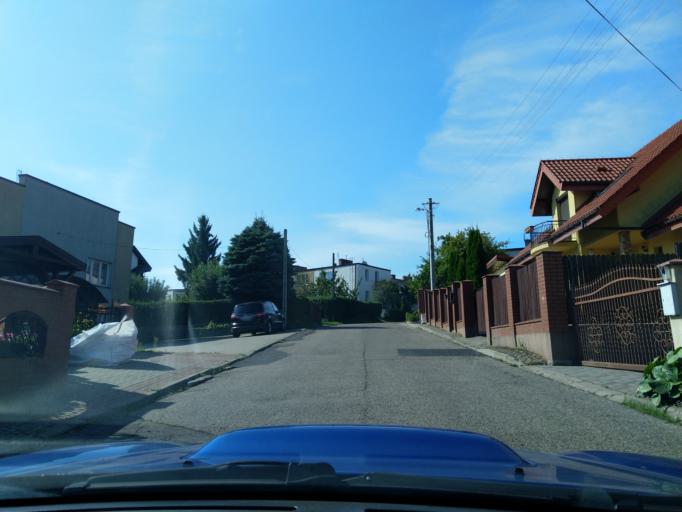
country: PL
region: Warmian-Masurian Voivodeship
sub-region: Olsztyn
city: Kortowo
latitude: 53.7695
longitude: 20.4397
